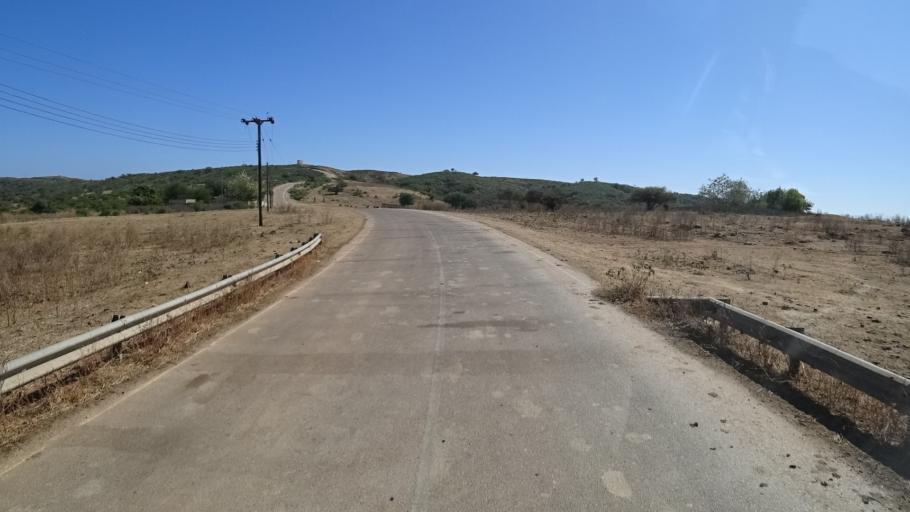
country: YE
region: Al Mahrah
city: Hawf
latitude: 16.7531
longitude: 53.3406
